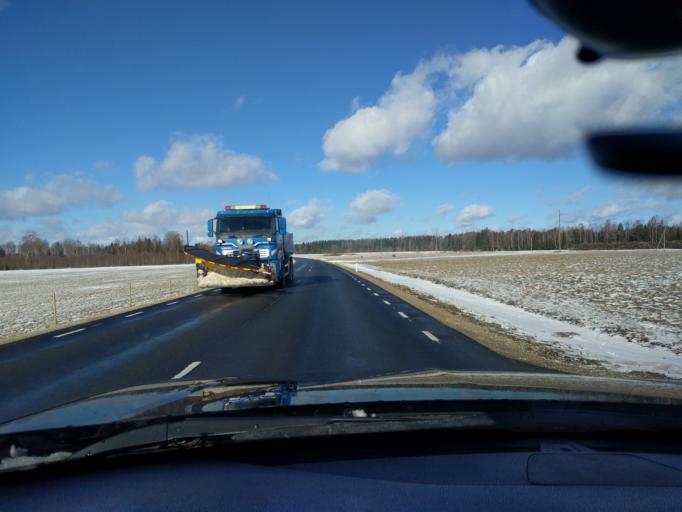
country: EE
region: Harju
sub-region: Anija vald
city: Kehra
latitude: 59.2713
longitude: 25.2961
